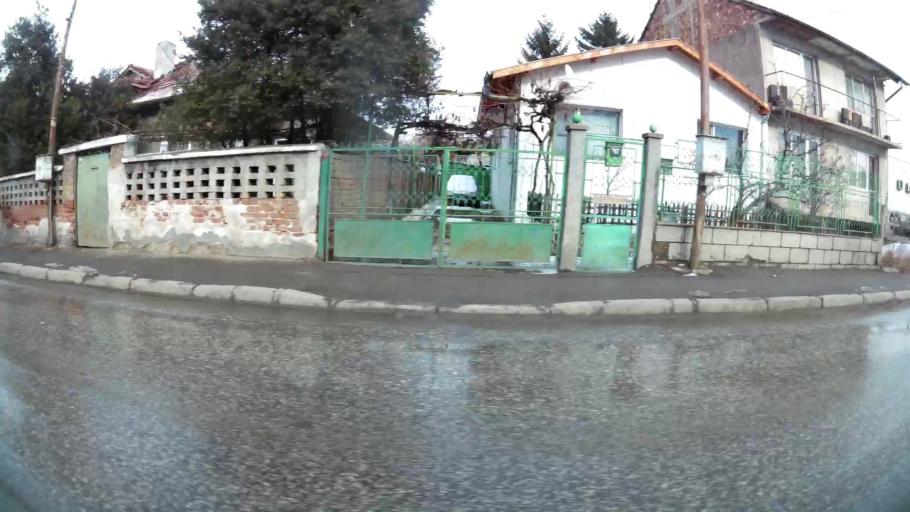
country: BG
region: Sofia-Capital
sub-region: Stolichna Obshtina
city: Sofia
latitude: 42.7056
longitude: 23.3849
